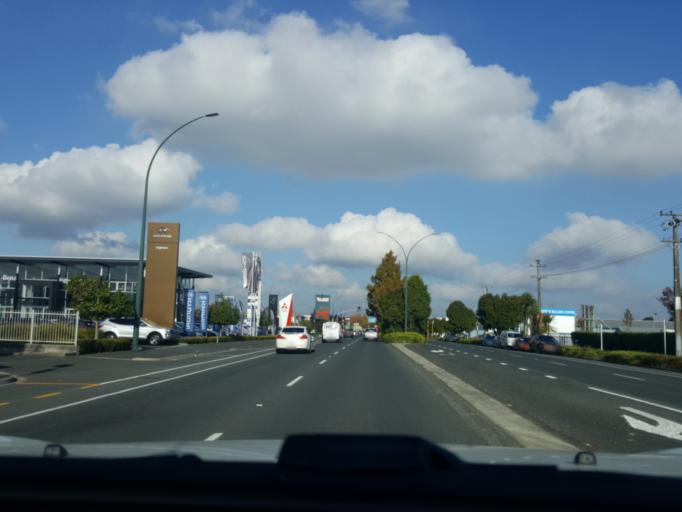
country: NZ
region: Waikato
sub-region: Hamilton City
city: Hamilton
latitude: -37.7613
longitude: 175.2498
